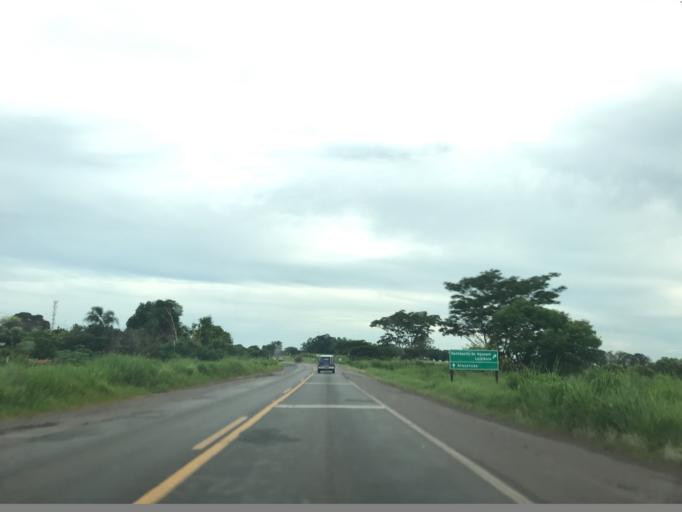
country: BR
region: Sao Paulo
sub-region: Tupa
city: Tupa
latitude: -21.6434
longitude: -50.5027
